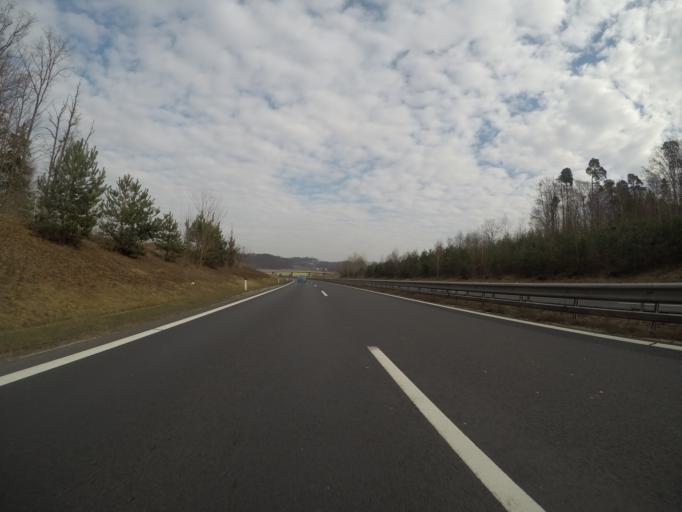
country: SI
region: Sveta Trojica v Slovenskih Goricah
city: Sv. Trojica v Slov. Goricah
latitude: 46.5551
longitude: 15.9001
